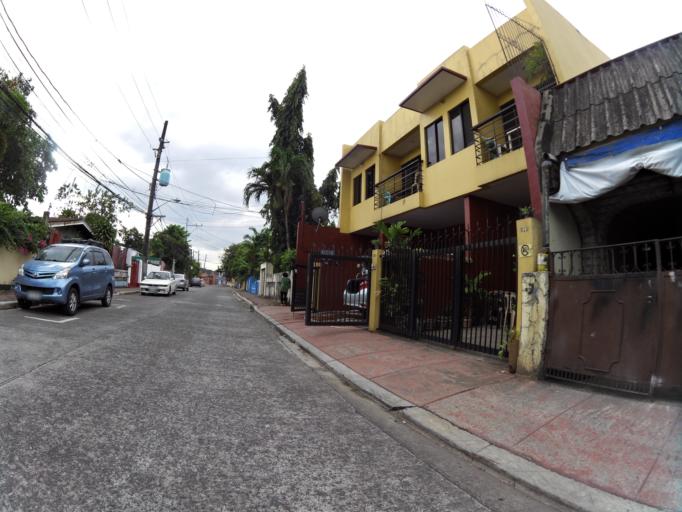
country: PH
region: Calabarzon
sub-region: Province of Rizal
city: Antipolo
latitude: 14.6398
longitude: 121.1144
